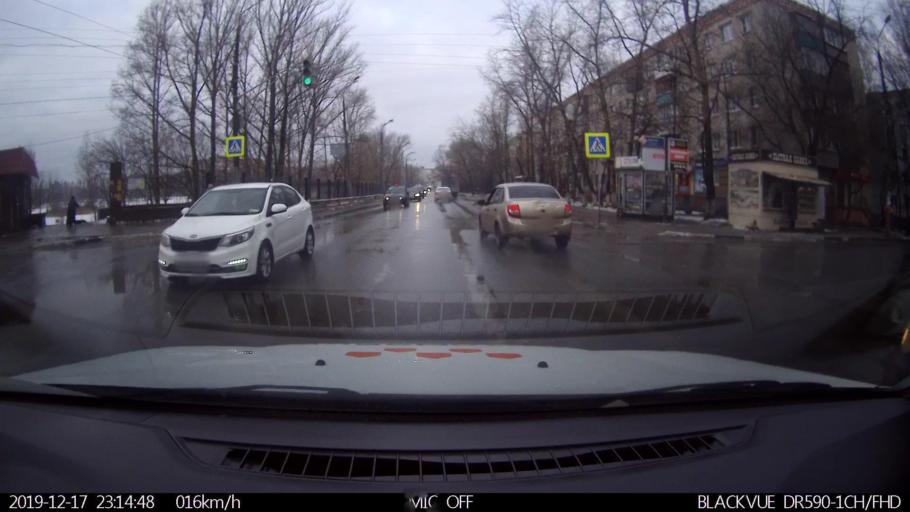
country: RU
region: Nizjnij Novgorod
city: Gorbatovka
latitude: 56.3556
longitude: 43.8299
